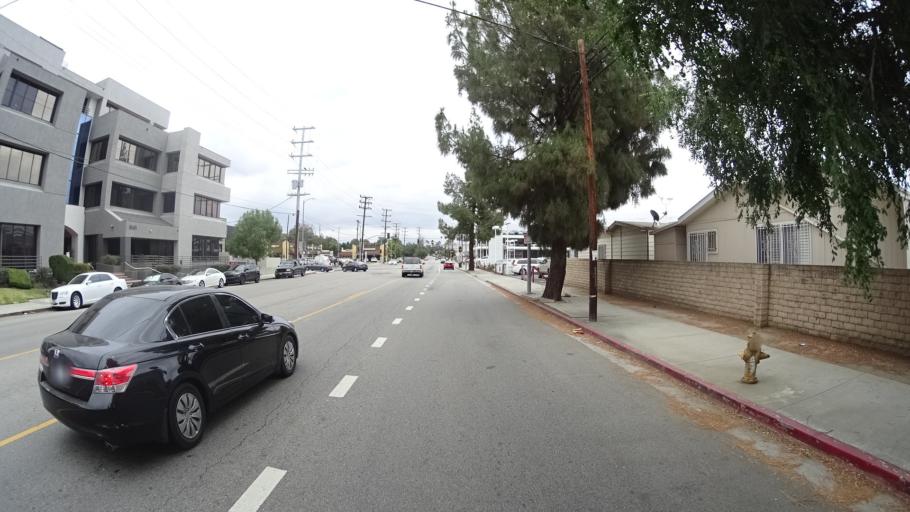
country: US
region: California
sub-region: Los Angeles County
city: San Fernando
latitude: 34.2719
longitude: -118.4689
